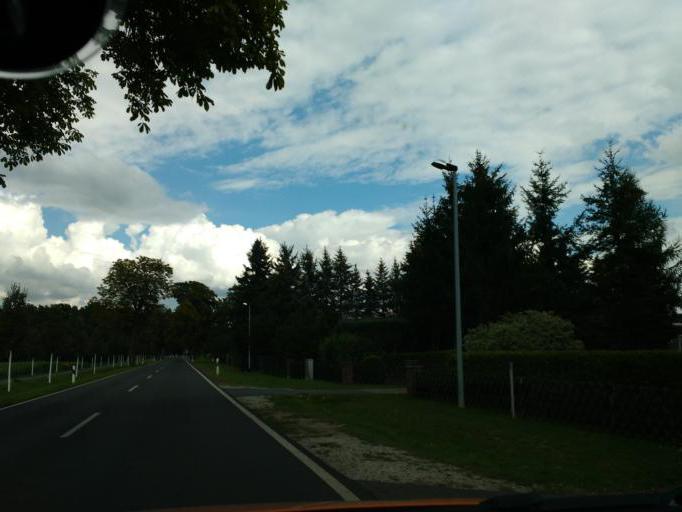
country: DE
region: Brandenburg
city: Wandlitz
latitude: 52.8080
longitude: 13.4917
